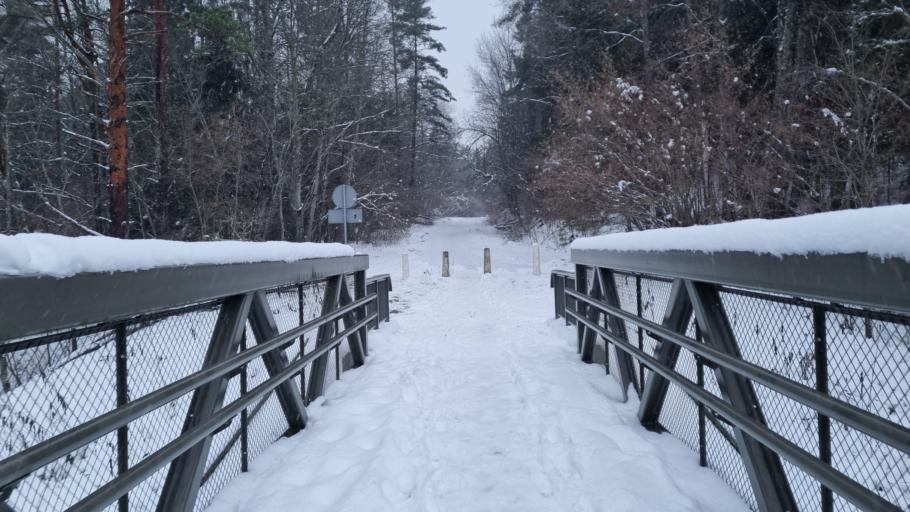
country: LV
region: Kuldigas Rajons
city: Kuldiga
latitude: 56.9952
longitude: 22.0095
